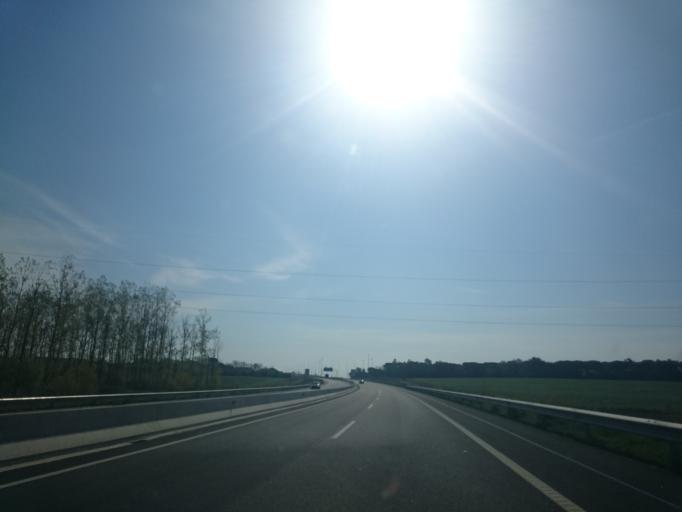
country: ES
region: Catalonia
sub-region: Provincia de Girona
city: Vilobi d'Onyar
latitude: 41.8694
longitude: 2.7680
